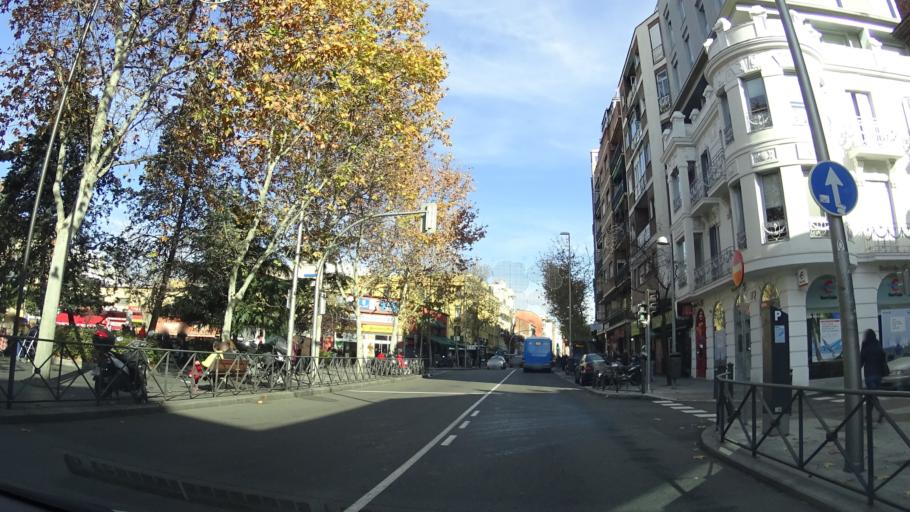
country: ES
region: Madrid
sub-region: Provincia de Madrid
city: Salamanca
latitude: 40.4438
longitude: -3.6745
